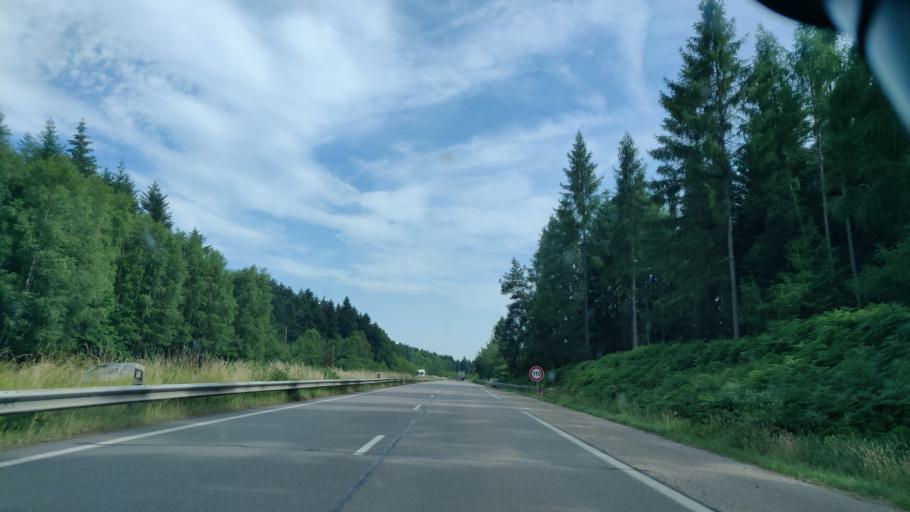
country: FR
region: Lorraine
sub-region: Departement des Vosges
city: Moyenmoutier
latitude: 48.3686
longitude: 6.8825
